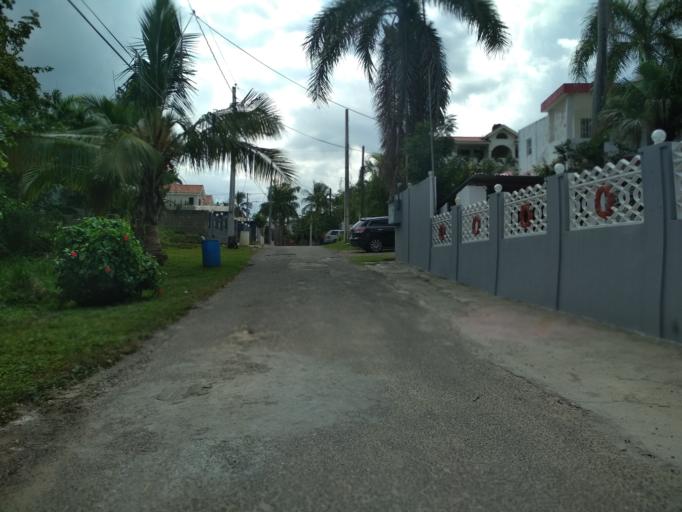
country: DO
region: Puerto Plata
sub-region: Puerto Plata
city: Puerto Plata
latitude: 19.8143
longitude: -70.7159
